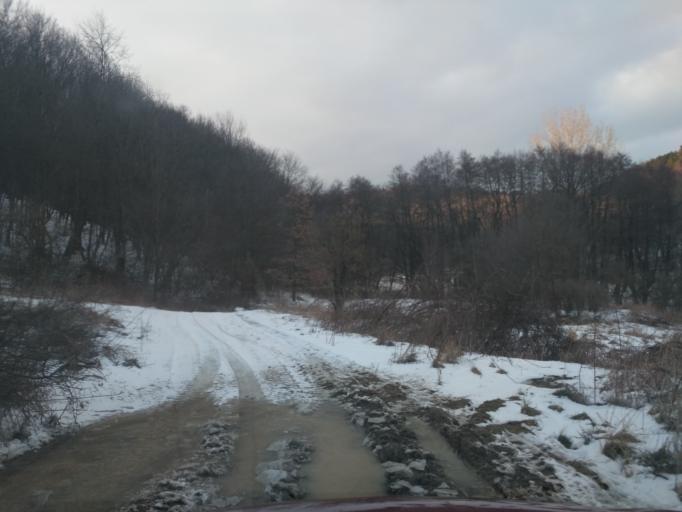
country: SK
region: Kosicky
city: Kosice
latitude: 48.7452
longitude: 21.1504
